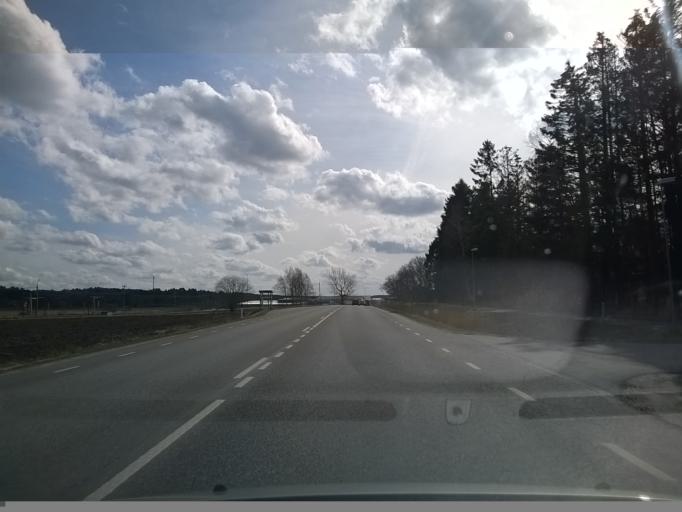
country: SE
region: Vaestra Goetaland
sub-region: Stenungsunds Kommun
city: Stora Hoga
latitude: 57.9923
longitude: 11.8296
